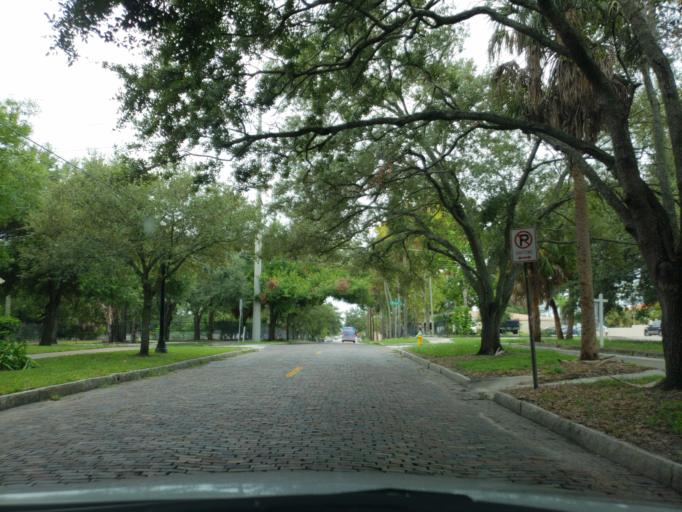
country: US
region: Florida
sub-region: Hillsborough County
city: Tampa
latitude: 27.9604
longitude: -82.4576
